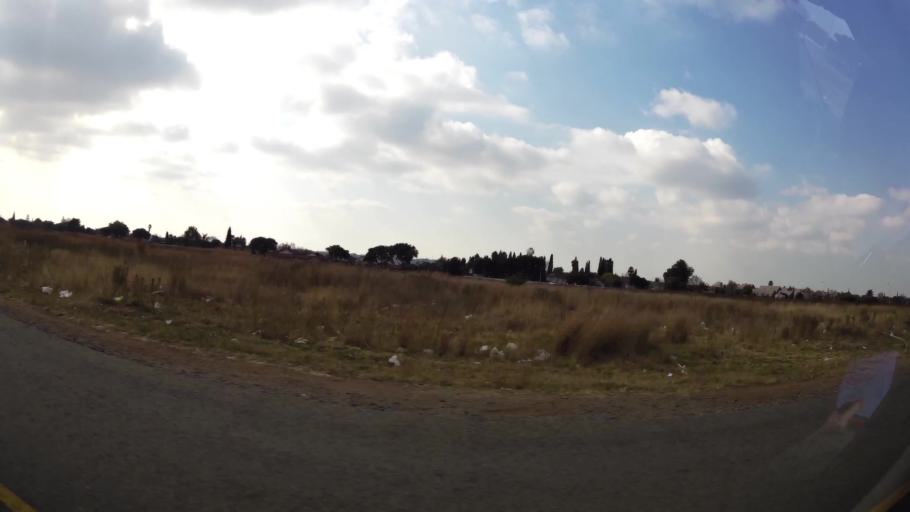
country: ZA
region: Gauteng
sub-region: Ekurhuleni Metropolitan Municipality
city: Benoni
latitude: -26.1580
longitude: 28.2767
